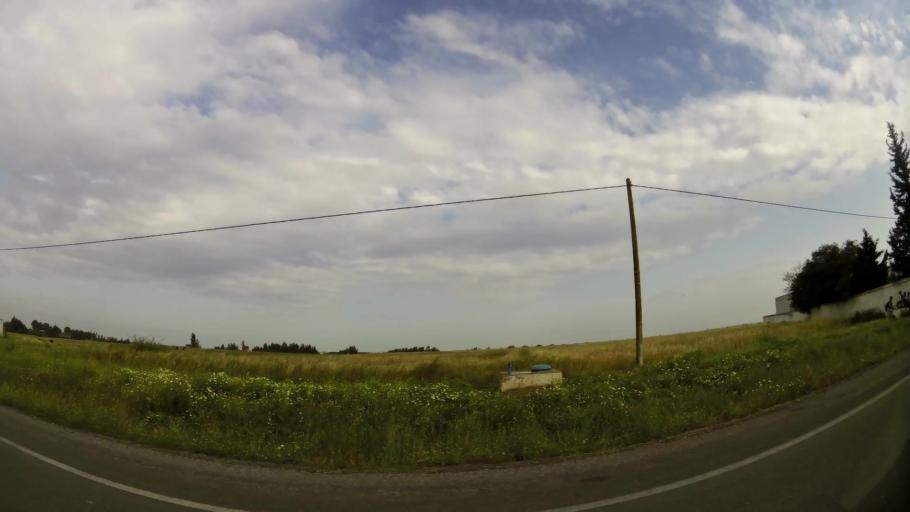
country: MA
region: Rabat-Sale-Zemmour-Zaer
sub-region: Khemisset
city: Khemisset
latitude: 33.7955
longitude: -6.1015
